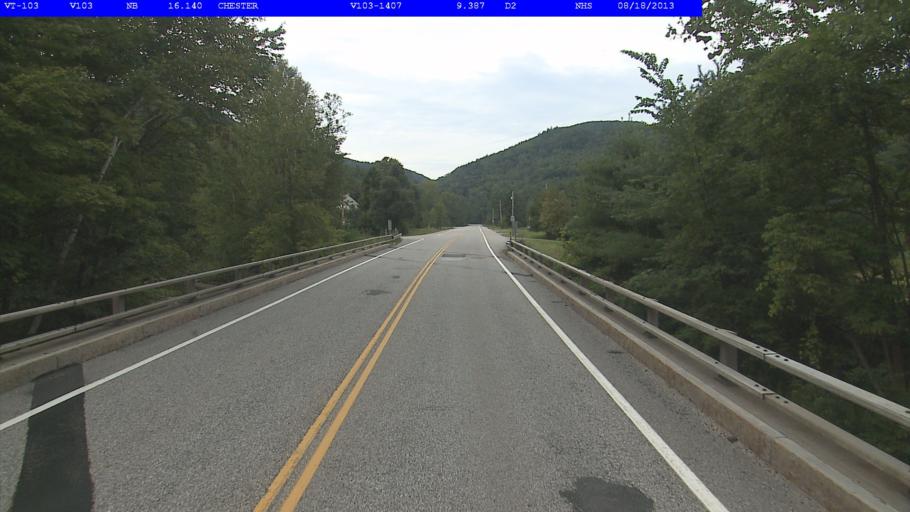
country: US
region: Vermont
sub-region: Windsor County
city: Chester
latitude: 43.3448
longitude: -72.6230
